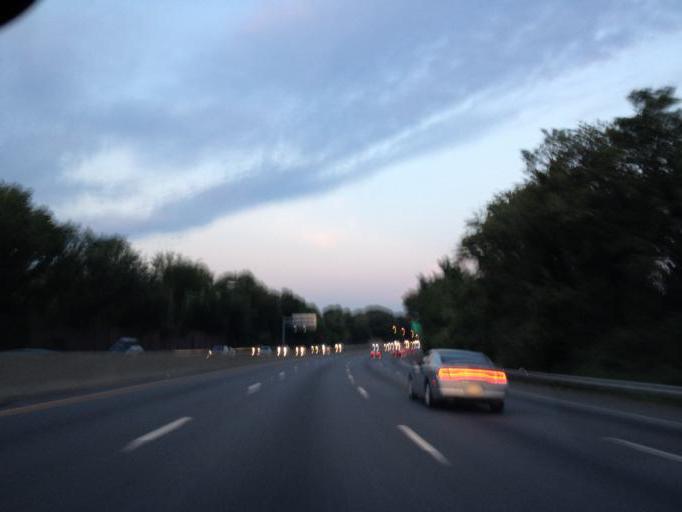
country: US
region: Maryland
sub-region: Montgomery County
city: Four Corners
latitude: 39.0168
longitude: -77.0264
